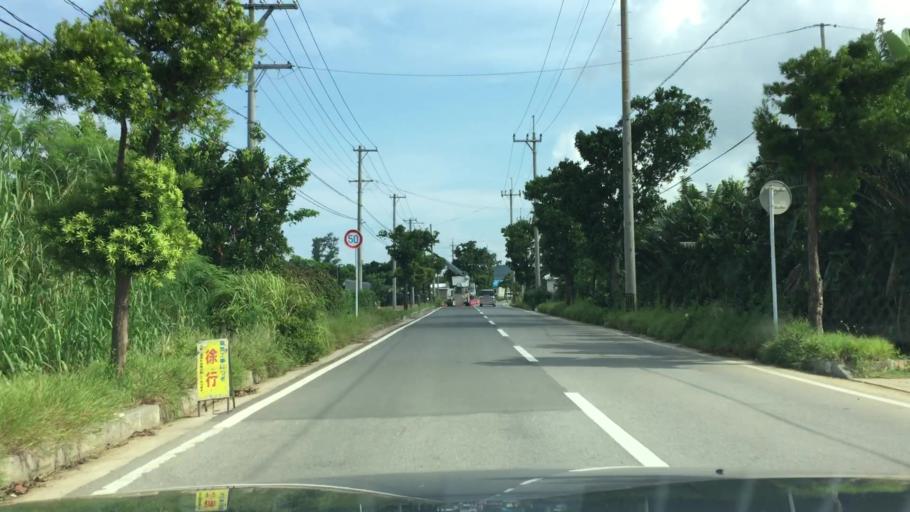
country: JP
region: Okinawa
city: Ishigaki
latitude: 24.4643
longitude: 124.2503
